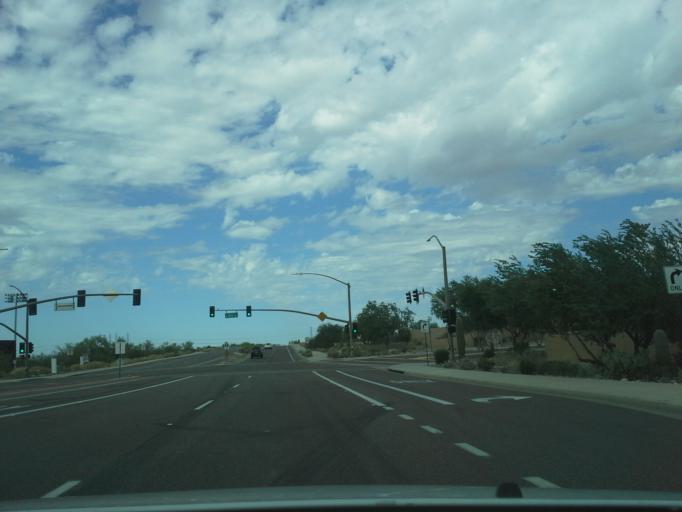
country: US
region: Arizona
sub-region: Maricopa County
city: Paradise Valley
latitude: 33.6402
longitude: -111.8691
